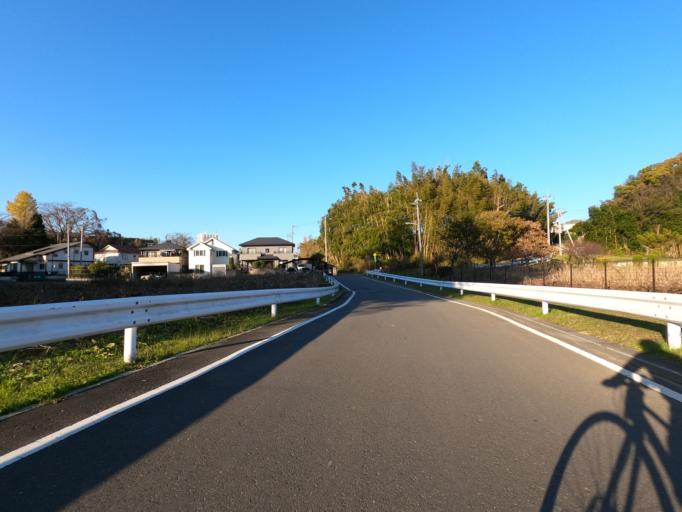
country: JP
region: Ibaraki
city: Moriya
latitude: 35.9443
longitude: 140.0008
